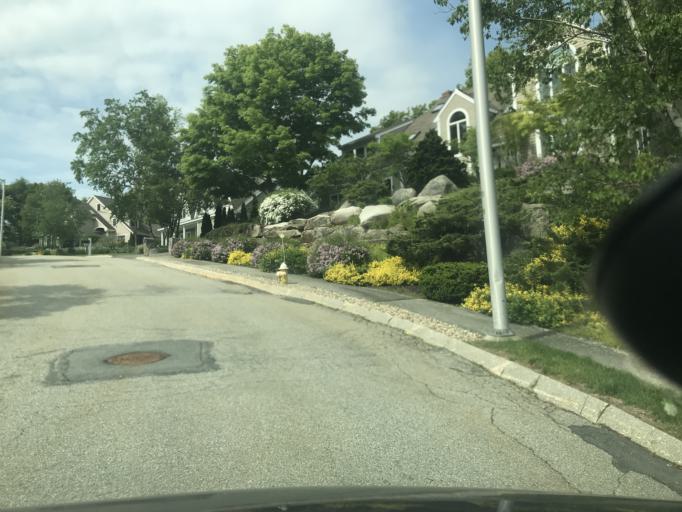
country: US
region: Massachusetts
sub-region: Essex County
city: Rockport
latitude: 42.6627
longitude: -70.6286
